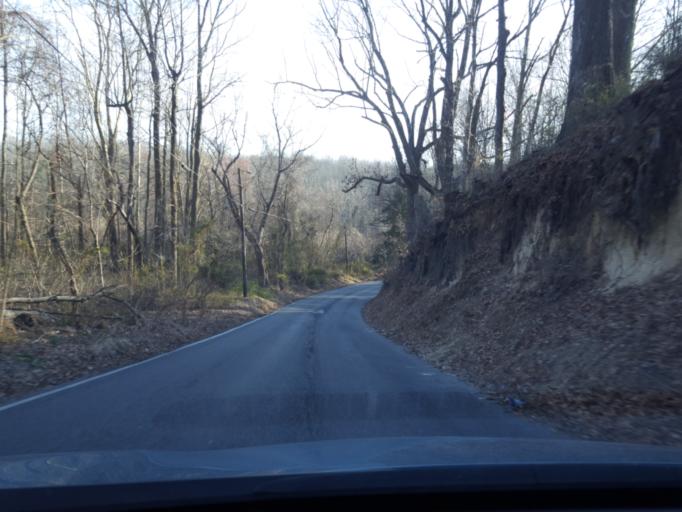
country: US
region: Maryland
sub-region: Anne Arundel County
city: Deale
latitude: 38.7703
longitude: -76.5747
